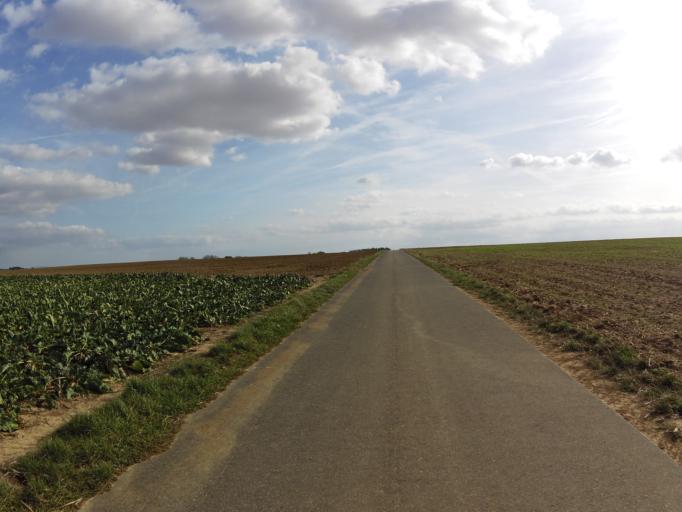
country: DE
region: Bavaria
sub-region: Regierungsbezirk Unterfranken
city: Eibelstadt
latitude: 49.7012
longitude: 9.9567
